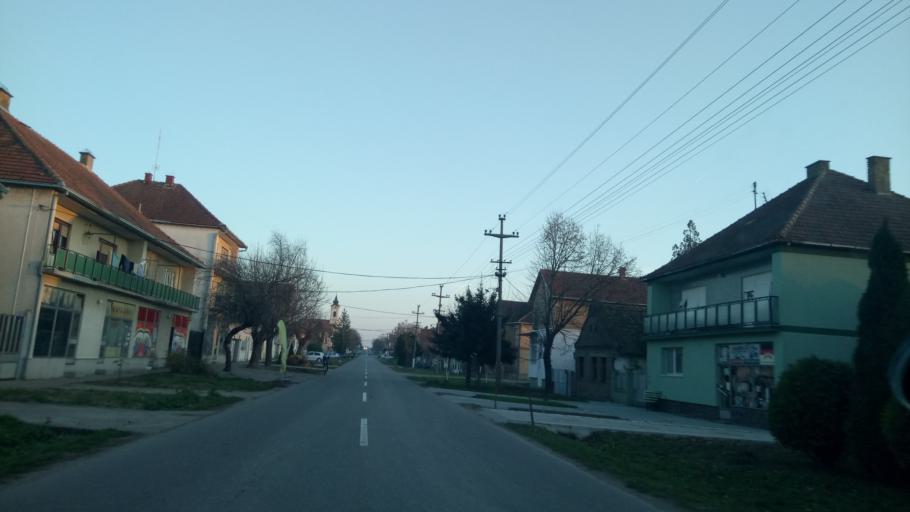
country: RS
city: Surduk
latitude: 45.0733
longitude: 20.3220
